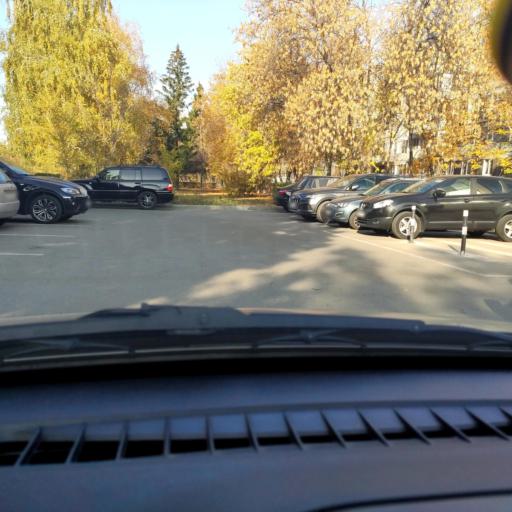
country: RU
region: Samara
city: Tol'yatti
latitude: 53.5171
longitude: 49.2862
